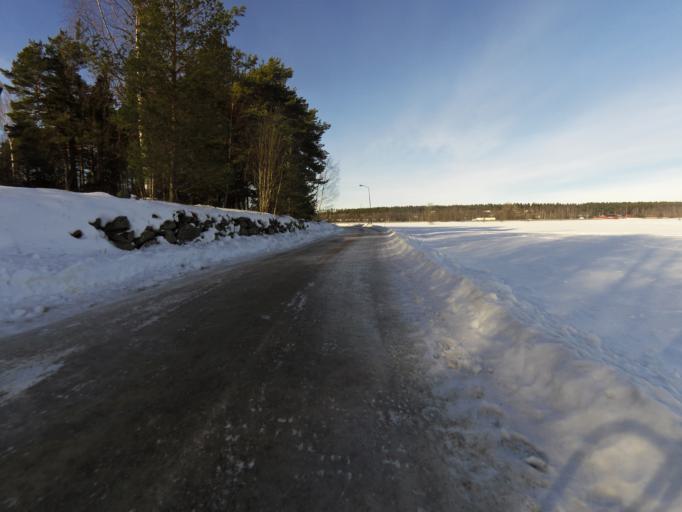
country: SE
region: Gaevleborg
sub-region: Gavle Kommun
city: Valbo
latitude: 60.6512
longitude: 17.0568
